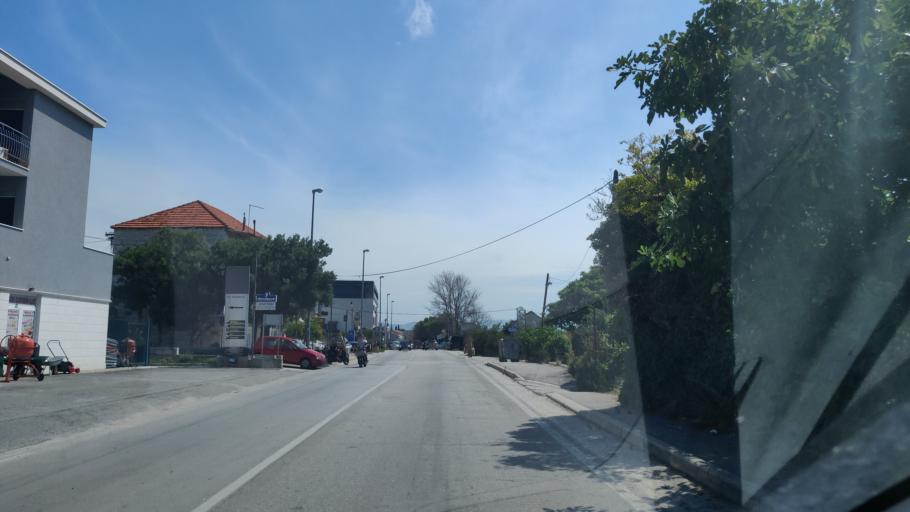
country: HR
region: Splitsko-Dalmatinska
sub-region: Grad Trogir
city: Trogir
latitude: 43.5176
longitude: 16.2414
